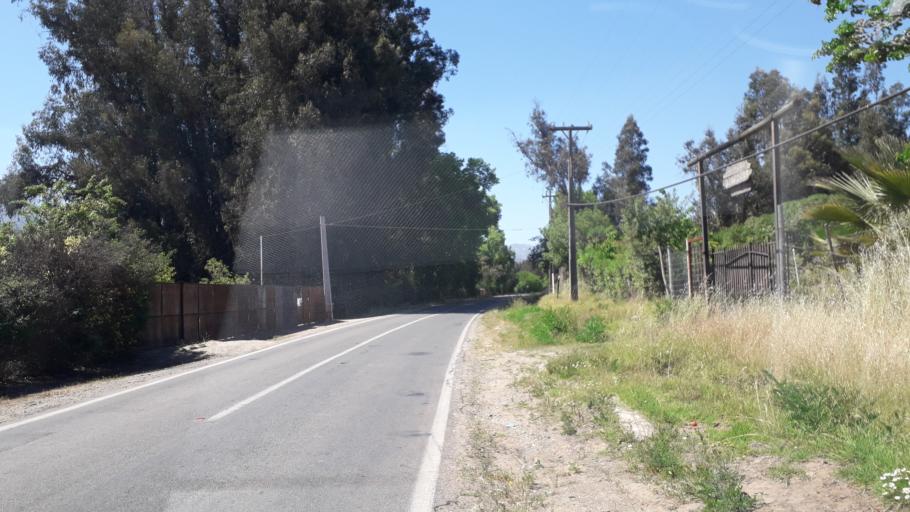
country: CL
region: Valparaiso
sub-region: Provincia de Marga Marga
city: Limache
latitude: -33.0403
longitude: -71.2320
